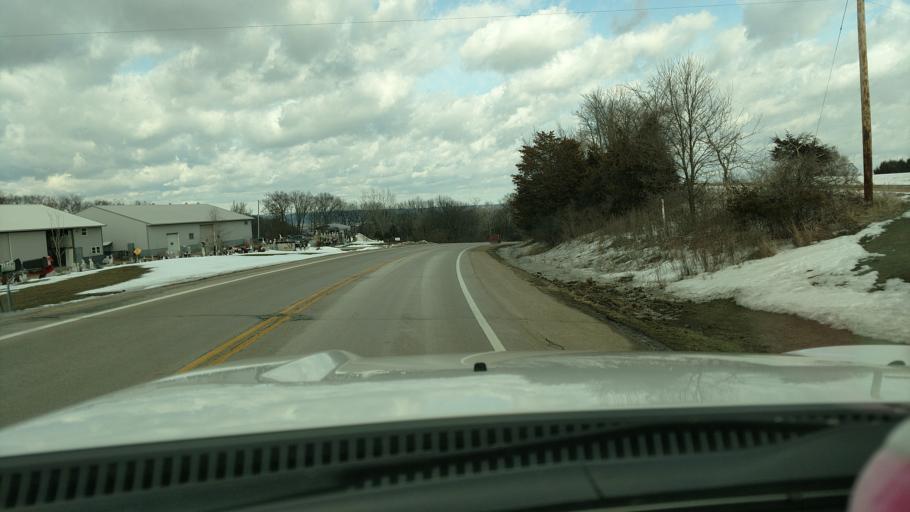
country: US
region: Minnesota
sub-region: Wabasha County
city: Wabasha
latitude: 44.2803
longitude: -92.0237
